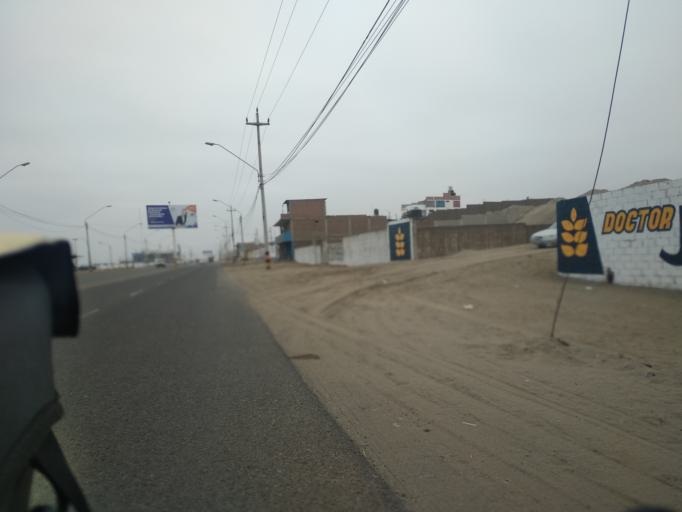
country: PE
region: La Libertad
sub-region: Provincia de Trujillo
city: Huanchaco
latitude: -8.0923
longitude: -79.1168
